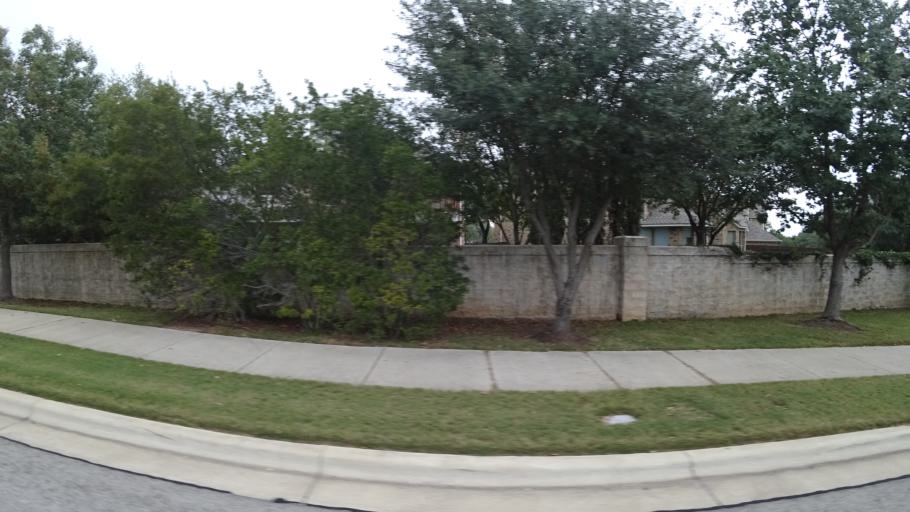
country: US
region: Texas
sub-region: Travis County
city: Bee Cave
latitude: 30.3468
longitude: -97.9103
